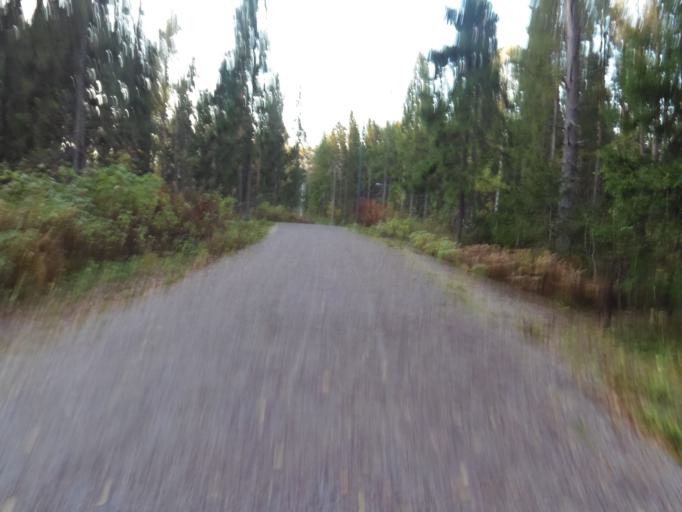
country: FI
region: Uusimaa
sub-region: Helsinki
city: Kauniainen
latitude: 60.2791
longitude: 24.7361
